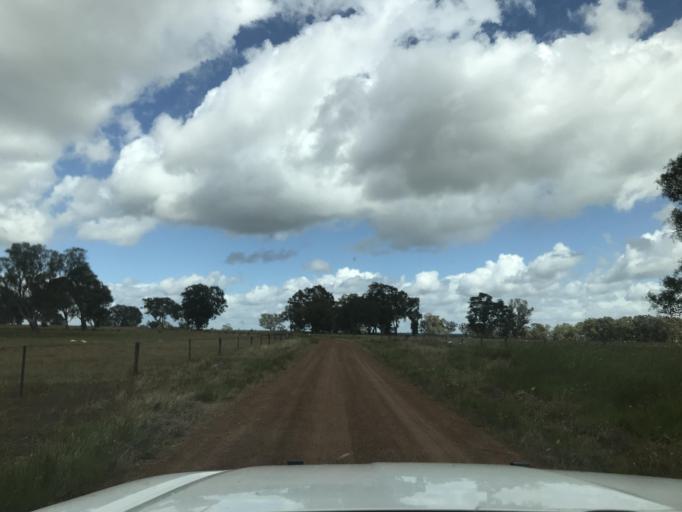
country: AU
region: South Australia
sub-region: Wattle Range
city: Penola
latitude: -37.1942
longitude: 141.4259
